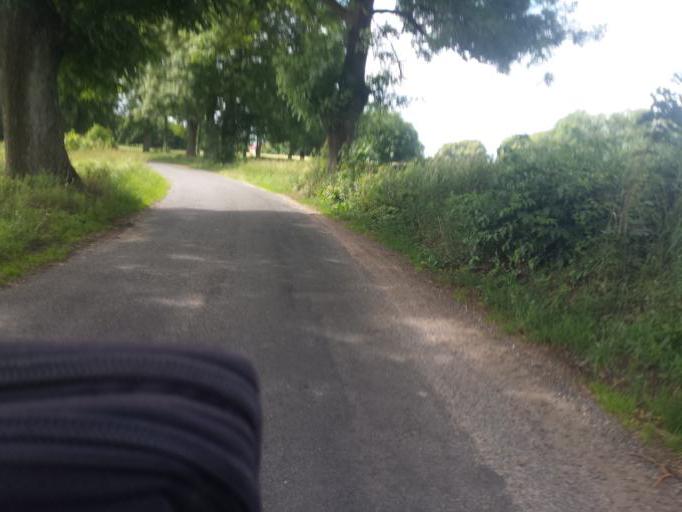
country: PL
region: Warmian-Masurian Voivodeship
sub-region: Powiat nowomiejski
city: Biskupiec
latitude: 53.5784
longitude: 19.4247
